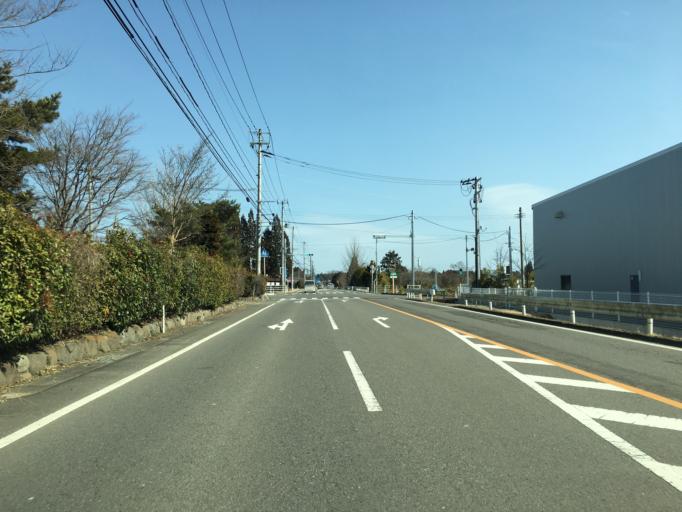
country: JP
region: Fukushima
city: Ishikawa
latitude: 37.1421
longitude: 140.3432
